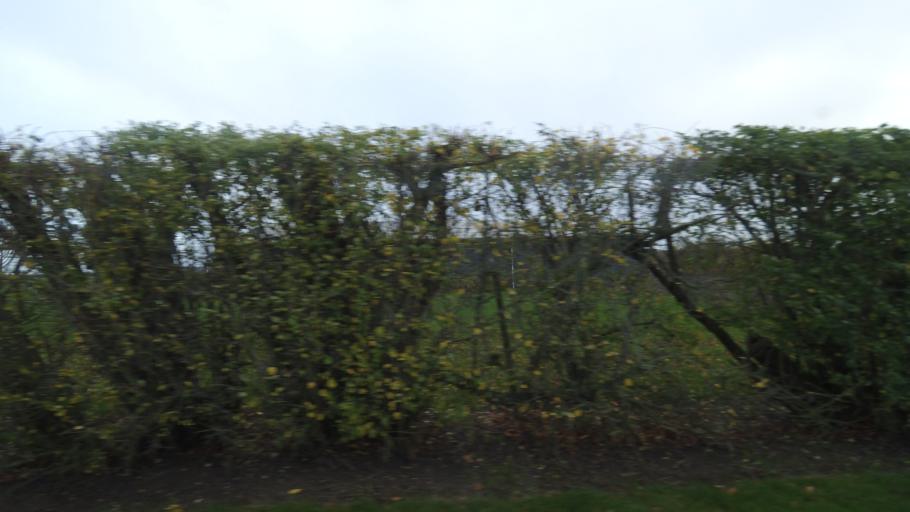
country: DK
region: Central Jutland
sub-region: Odder Kommune
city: Odder
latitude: 55.9103
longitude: 10.2080
